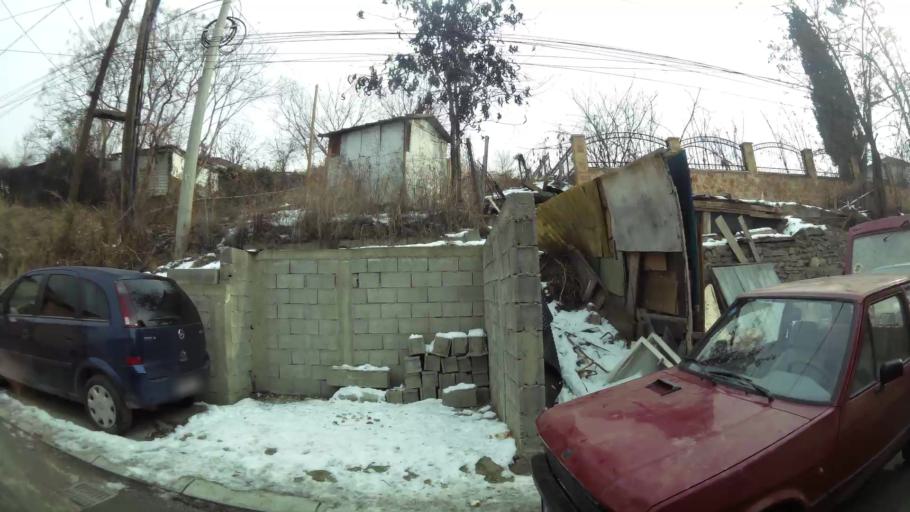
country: MK
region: Cair
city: Cair
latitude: 42.0076
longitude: 21.4467
